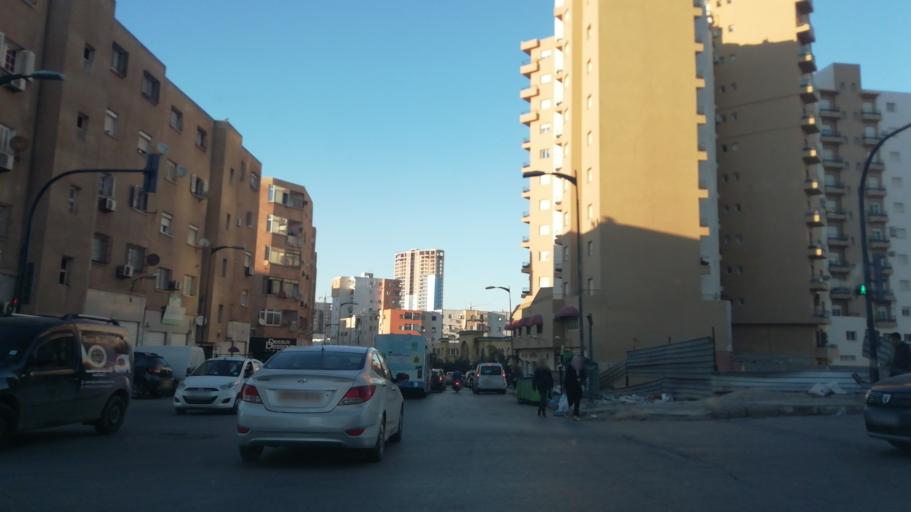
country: DZ
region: Oran
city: Bir el Djir
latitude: 35.7226
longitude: -0.5876
